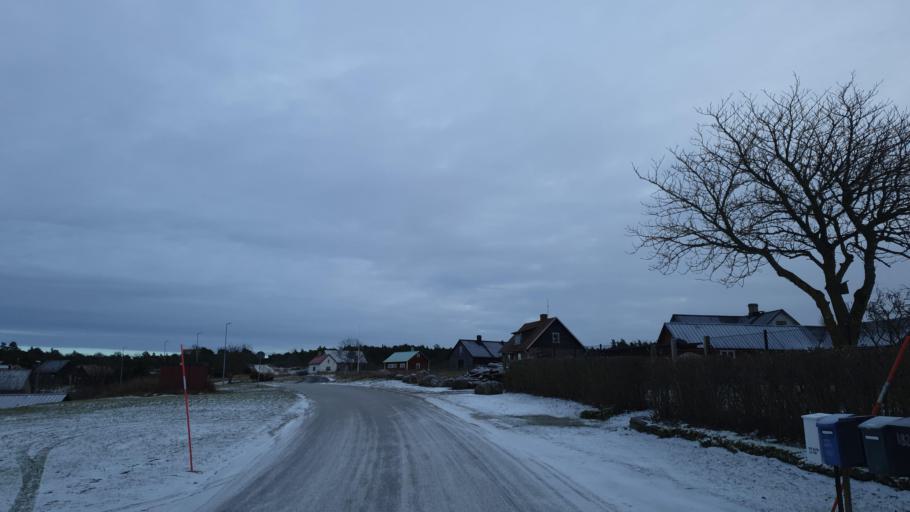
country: SE
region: Gotland
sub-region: Gotland
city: Slite
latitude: 57.4209
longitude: 18.9134
